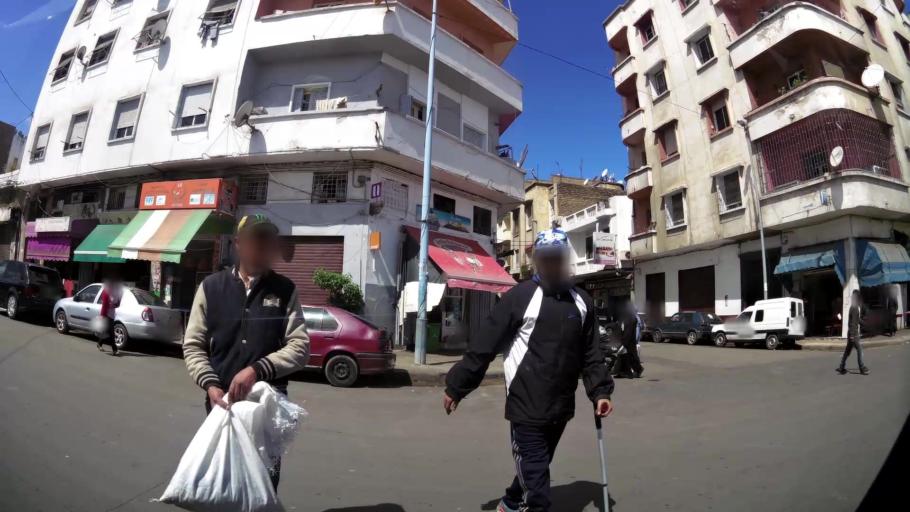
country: MA
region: Grand Casablanca
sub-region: Casablanca
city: Casablanca
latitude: 33.5964
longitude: -7.6244
